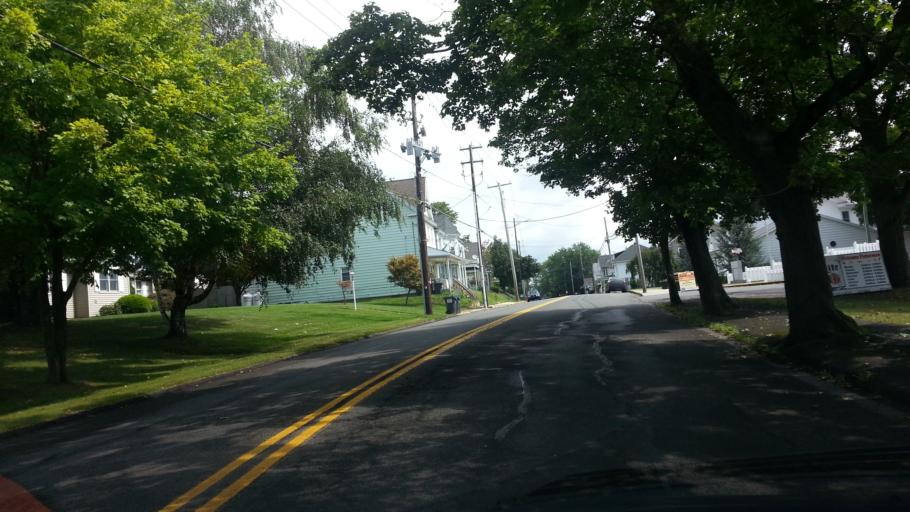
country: US
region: Pennsylvania
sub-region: Schuylkill County
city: Shenandoah Heights
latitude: 40.8567
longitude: -76.2409
